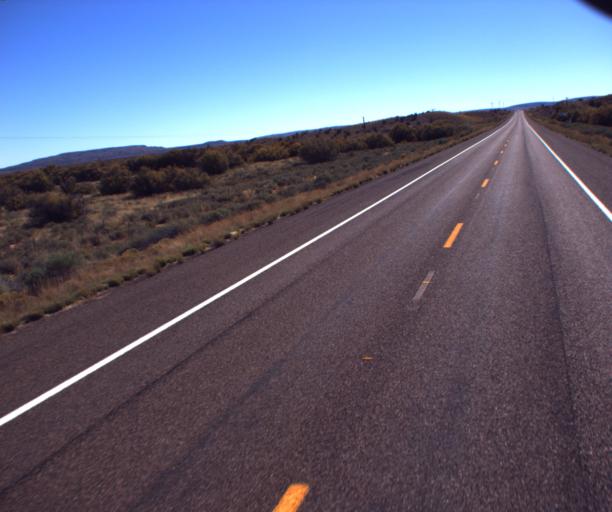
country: US
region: Arizona
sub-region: Apache County
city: Saint Johns
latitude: 34.6311
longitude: -109.6789
